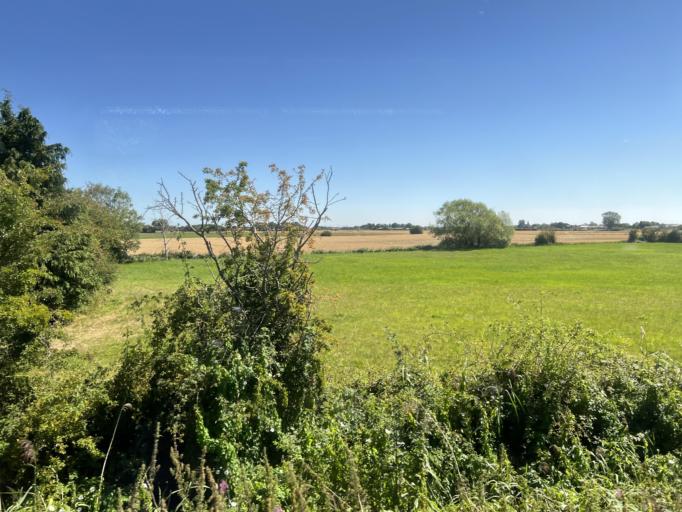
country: GB
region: England
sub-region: Lincolnshire
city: Spilsby
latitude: 53.1376
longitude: 0.1587
